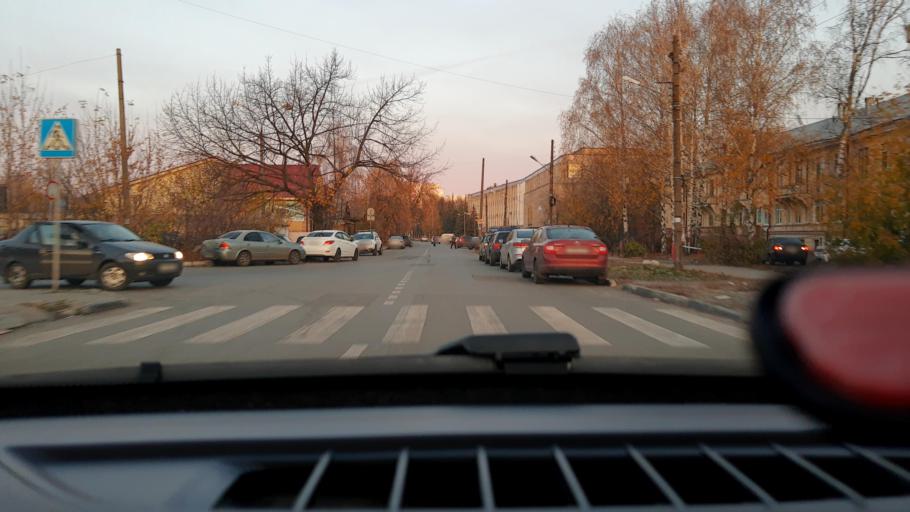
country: RU
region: Nizjnij Novgorod
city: Neklyudovo
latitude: 56.3595
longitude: 43.8698
